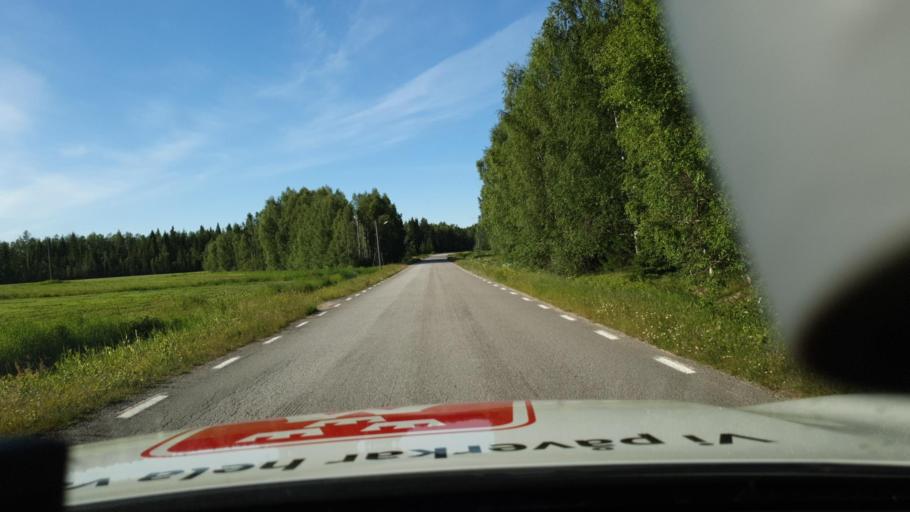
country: SE
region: Norrbotten
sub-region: Kalix Kommun
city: Toere
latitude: 65.8581
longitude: 22.6765
